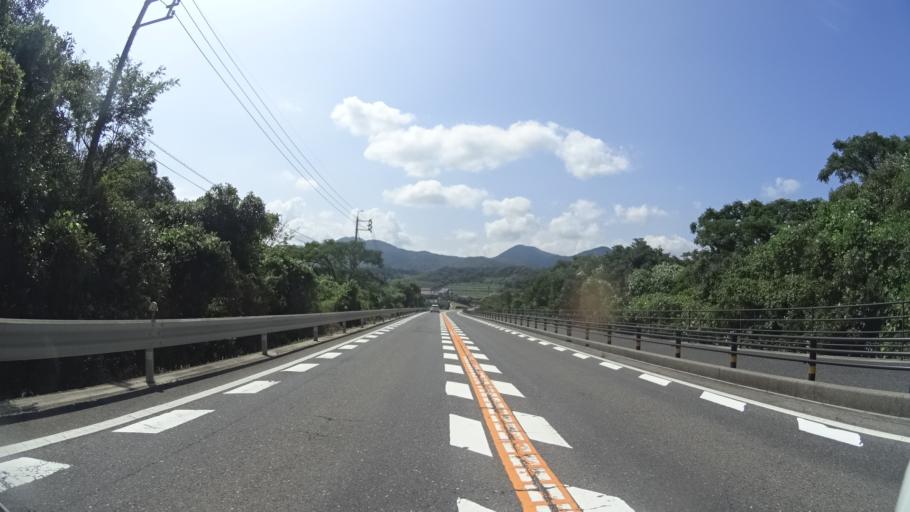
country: JP
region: Shimane
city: Masuda
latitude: 34.6744
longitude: 131.7530
